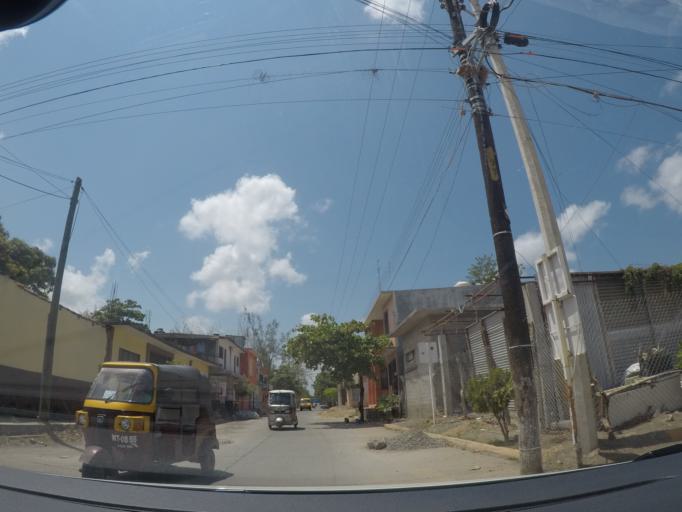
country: MX
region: Oaxaca
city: Juchitan de Zaragoza
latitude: 16.4384
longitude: -95.0179
